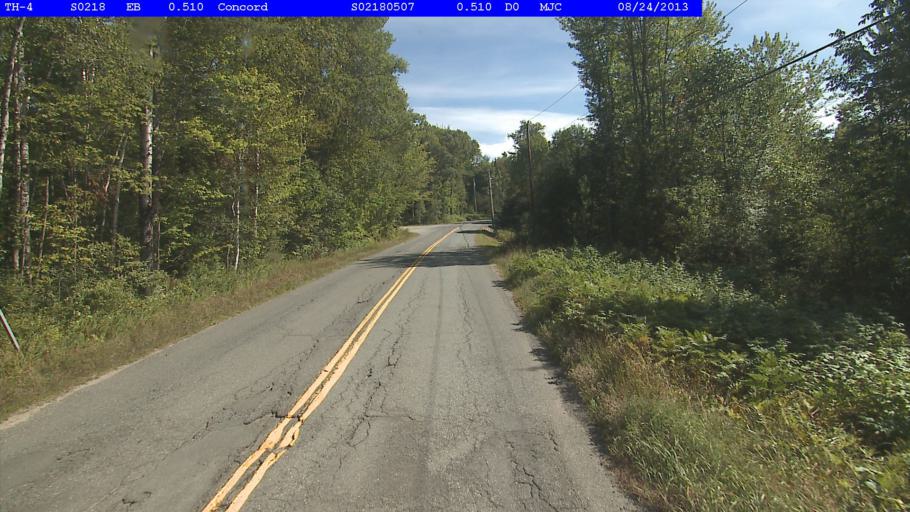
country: US
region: New Hampshire
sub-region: Grafton County
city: Littleton
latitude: 44.4581
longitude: -71.7711
